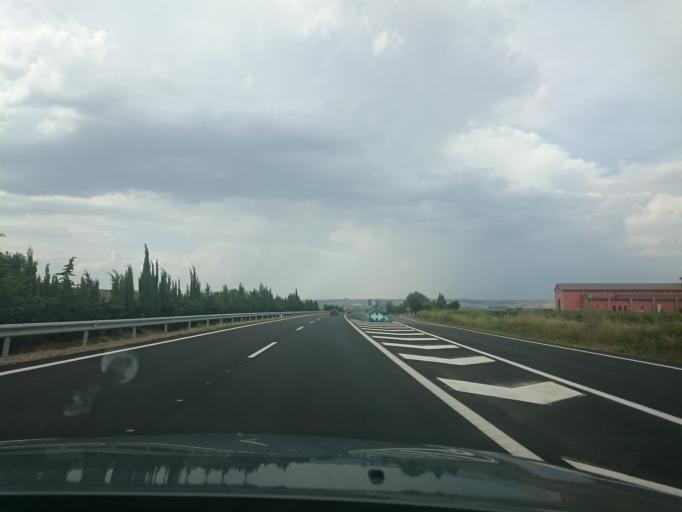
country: ES
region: La Rioja
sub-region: Provincia de La Rioja
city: Aldeanueva de Ebro
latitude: 42.2343
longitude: -1.9011
